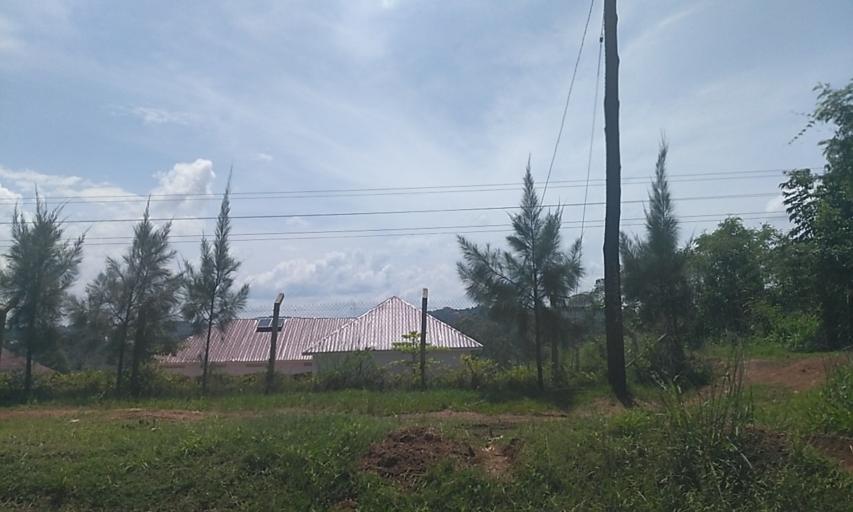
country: UG
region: Central Region
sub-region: Wakiso District
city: Wakiso
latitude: 0.4133
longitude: 32.4525
